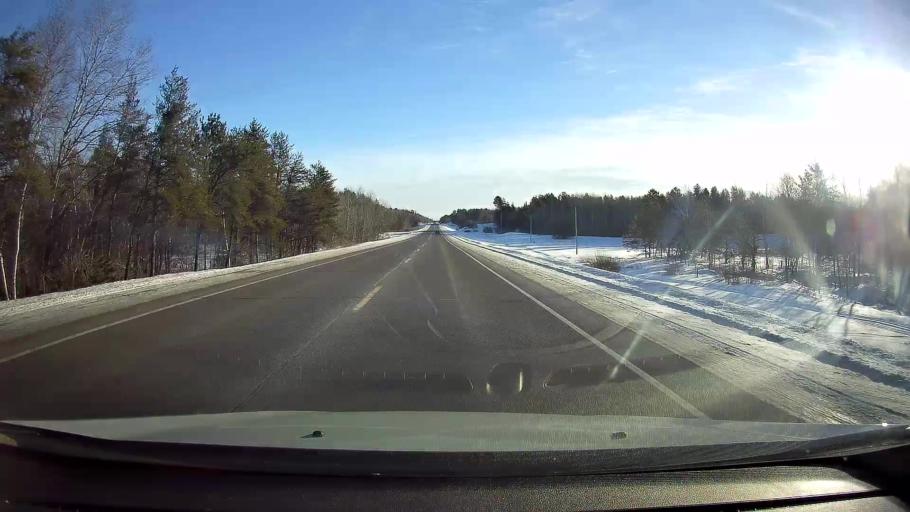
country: US
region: Wisconsin
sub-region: Washburn County
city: Spooner
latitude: 45.9104
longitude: -91.7962
